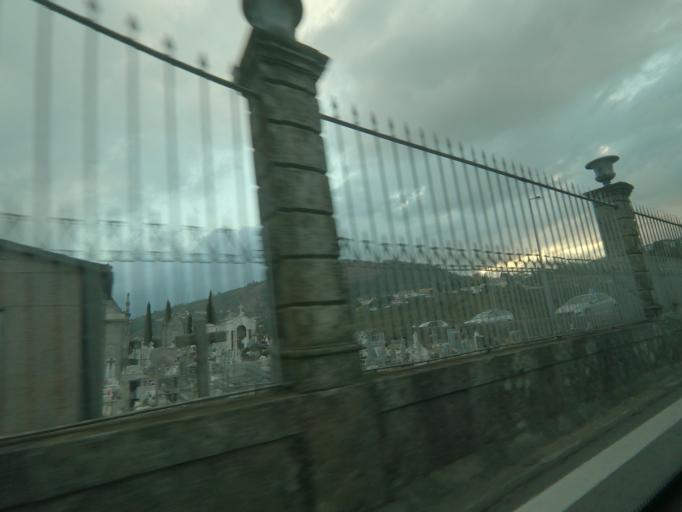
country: PT
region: Vila Real
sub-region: Mesao Frio
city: Mesao Frio
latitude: 41.1566
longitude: -7.8869
